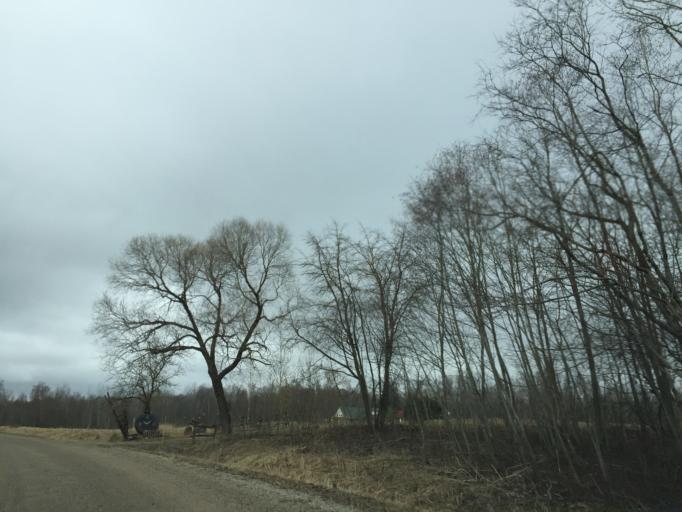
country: LV
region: Ilukste
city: Ilukste
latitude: 56.0221
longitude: 26.2328
